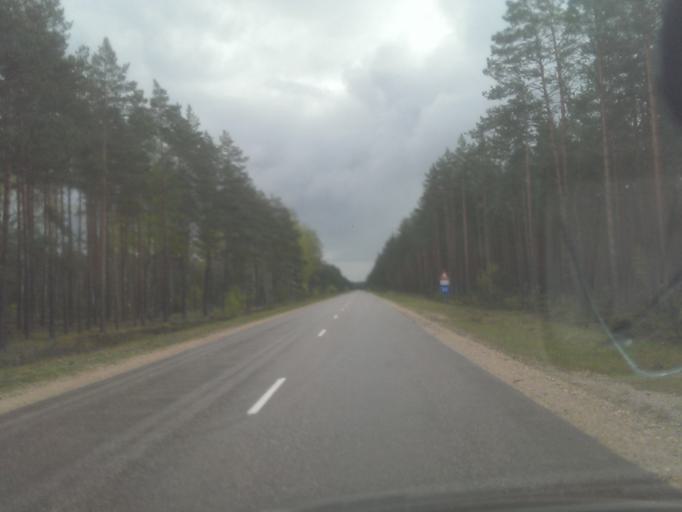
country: LV
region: Ventspils Rajons
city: Piltene
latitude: 57.1311
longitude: 21.7303
